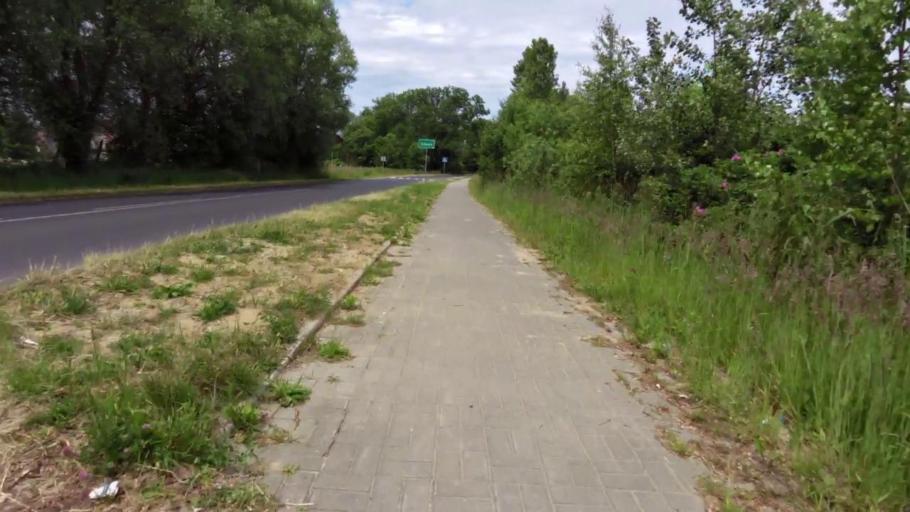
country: PL
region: West Pomeranian Voivodeship
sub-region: Powiat kamienski
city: Kamien Pomorski
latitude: 53.9891
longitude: 14.6881
